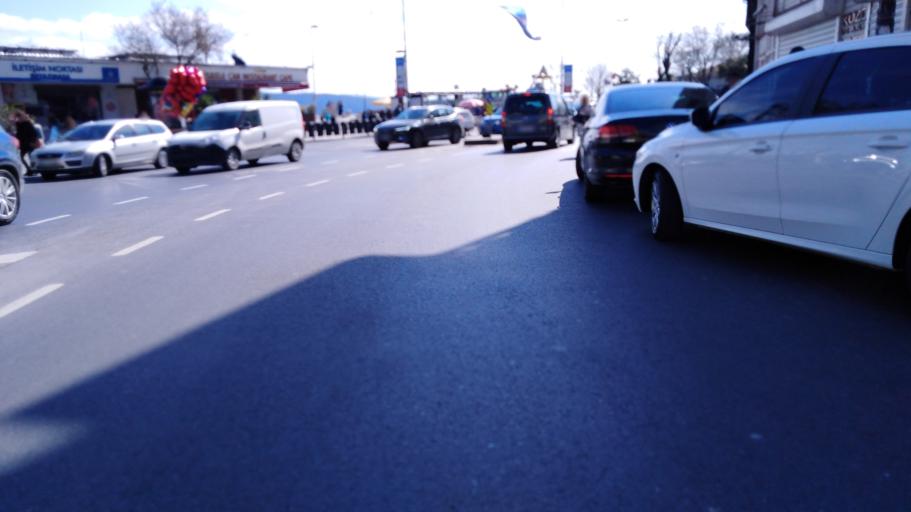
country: TR
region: Istanbul
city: Arikoey
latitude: 41.1675
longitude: 29.0571
